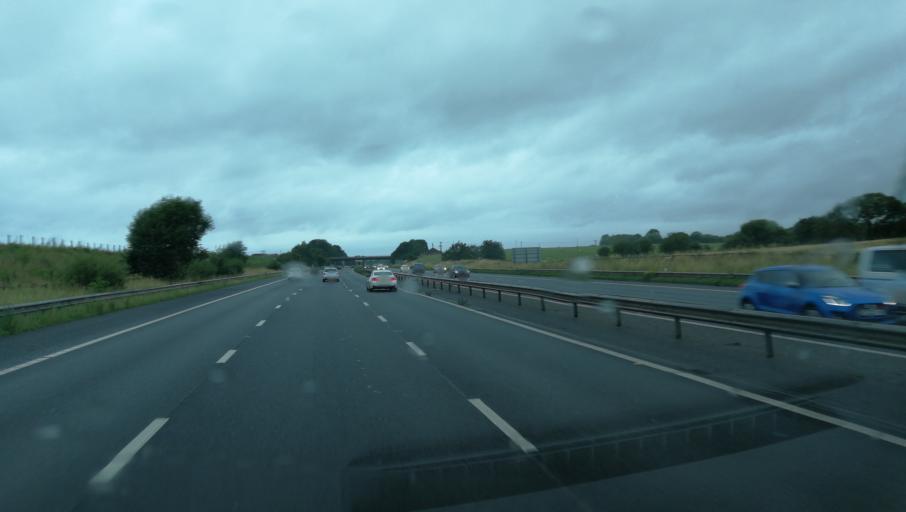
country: GB
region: England
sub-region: Borough of Bolton
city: Westhoughton
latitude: 53.5671
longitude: -2.5295
